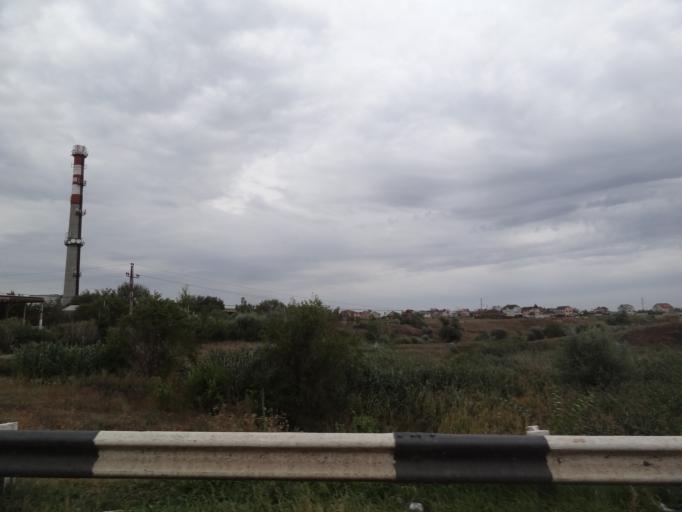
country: RU
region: Saratov
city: Shumeyka
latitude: 51.5085
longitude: 46.2006
